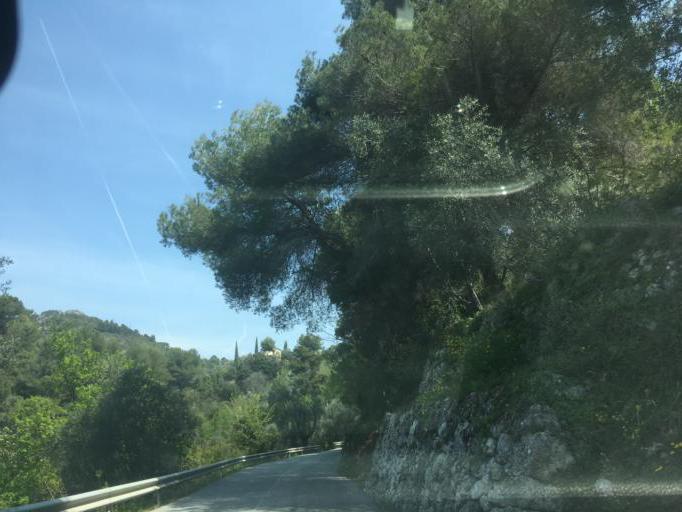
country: FR
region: Provence-Alpes-Cote d'Azur
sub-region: Departement des Alpes-Maritimes
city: Saint-Martin-du-Var
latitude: 43.8292
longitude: 7.1953
